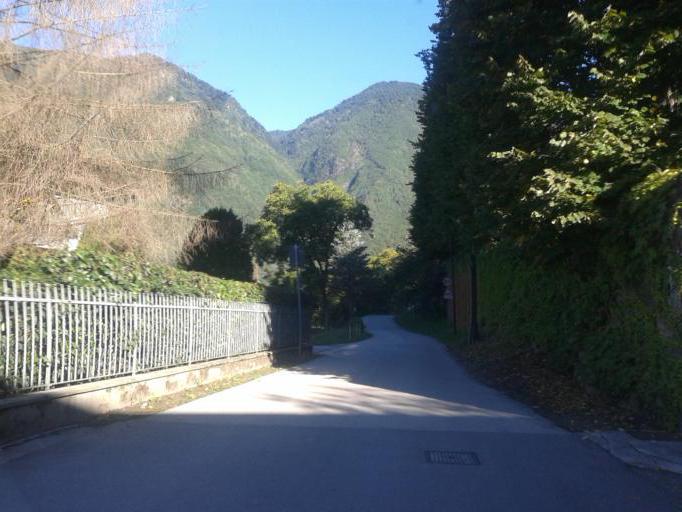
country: IT
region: Trentino-Alto Adige
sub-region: Provincia di Trento
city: Storo
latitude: 45.8532
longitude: 10.5770
